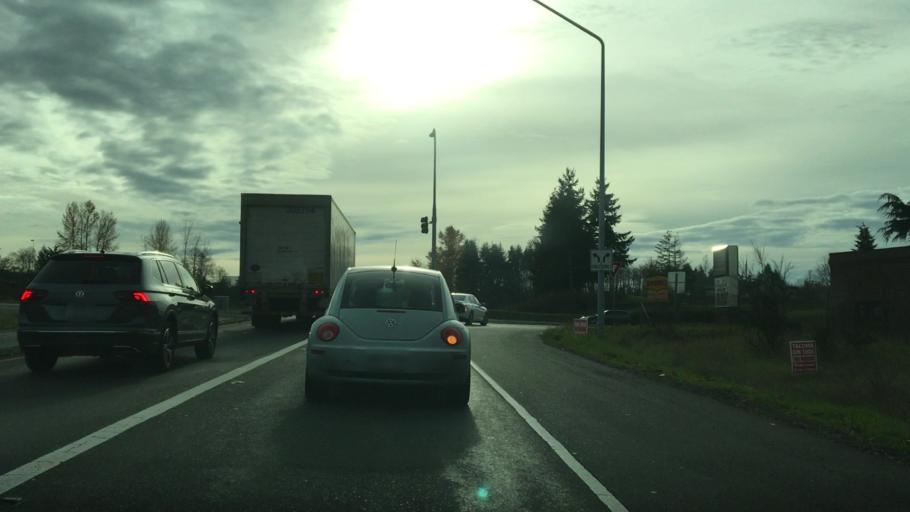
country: US
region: Washington
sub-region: Pierce County
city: Puyallup
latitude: 47.1621
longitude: -122.2985
